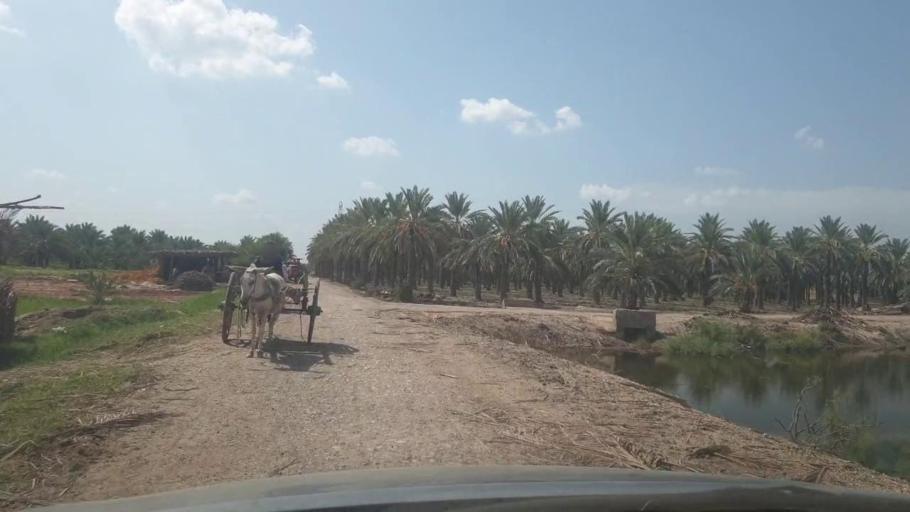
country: PK
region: Sindh
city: Khairpur
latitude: 27.5496
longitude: 68.8129
